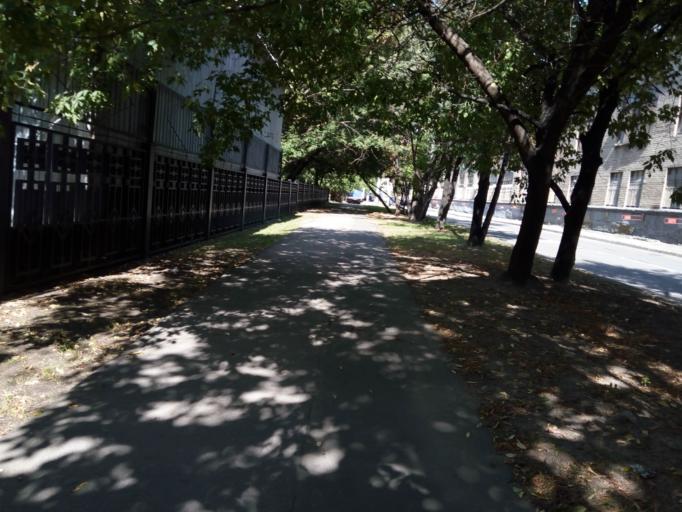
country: RU
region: Moscow
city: Sokol
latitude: 55.7768
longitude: 37.5355
